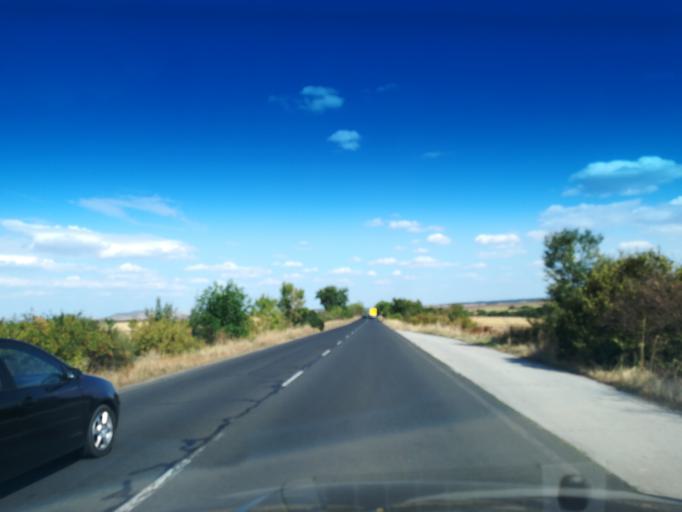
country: BG
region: Stara Zagora
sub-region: Obshtina Chirpan
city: Chirpan
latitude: 42.0573
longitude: 25.2919
